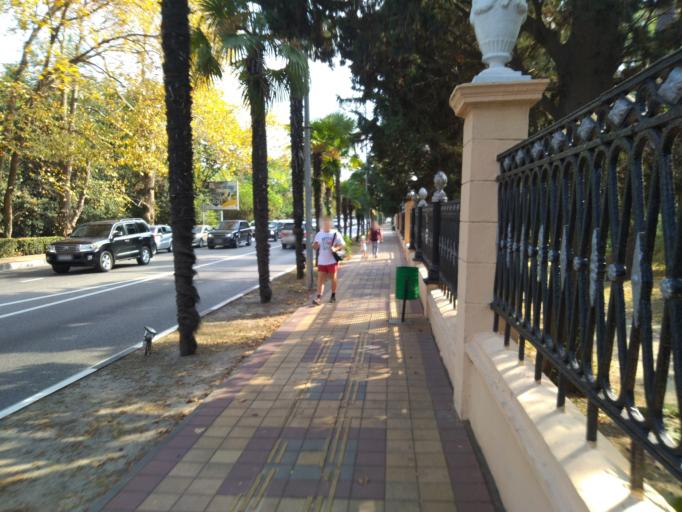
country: RU
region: Krasnodarskiy
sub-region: Sochi City
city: Sochi
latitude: 43.5928
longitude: 39.7174
